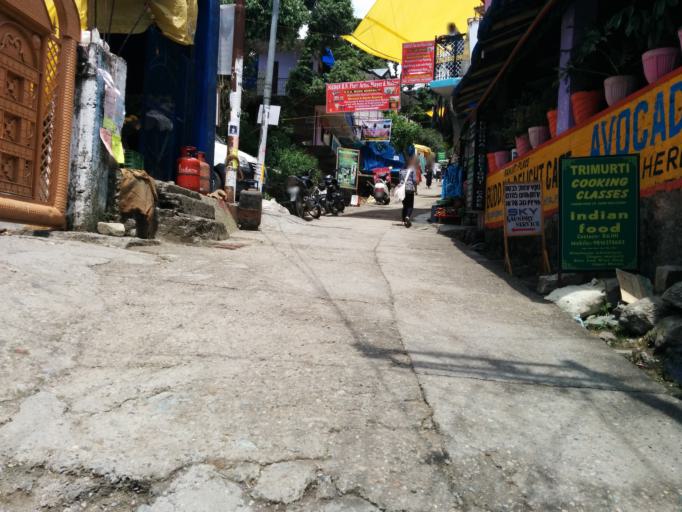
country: IN
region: Himachal Pradesh
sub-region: Kangra
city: Dharmsala
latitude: 32.2451
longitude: 76.3325
